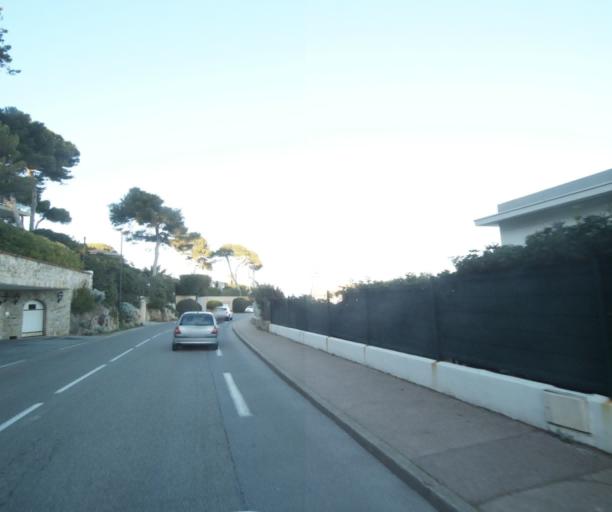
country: FR
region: Provence-Alpes-Cote d'Azur
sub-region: Departement des Alpes-Maritimes
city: Antibes
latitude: 43.5681
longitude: 7.1385
